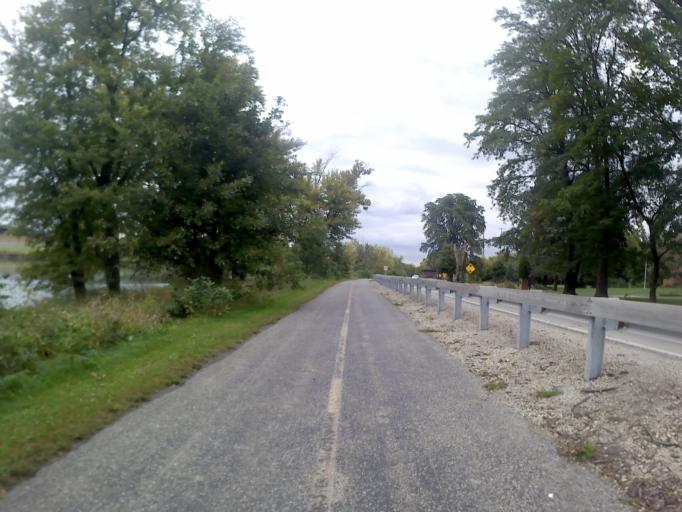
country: US
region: Illinois
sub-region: Kendall County
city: Boulder Hill
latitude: 41.7136
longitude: -88.3496
